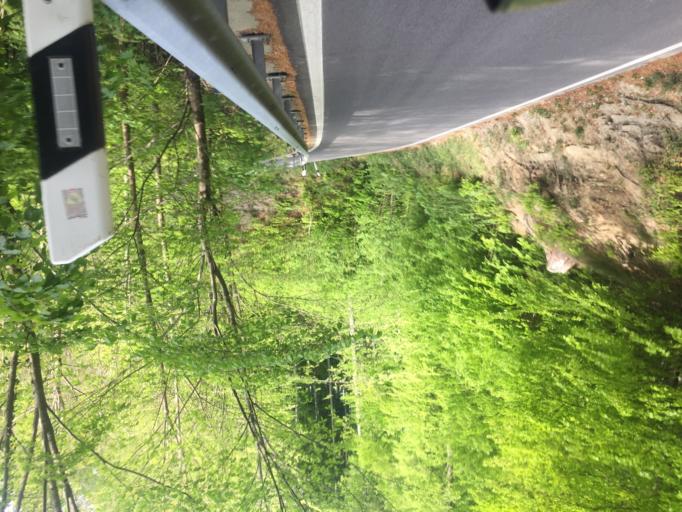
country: CH
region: Bern
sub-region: Bern-Mittelland District
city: Belp
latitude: 46.8751
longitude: 7.5077
